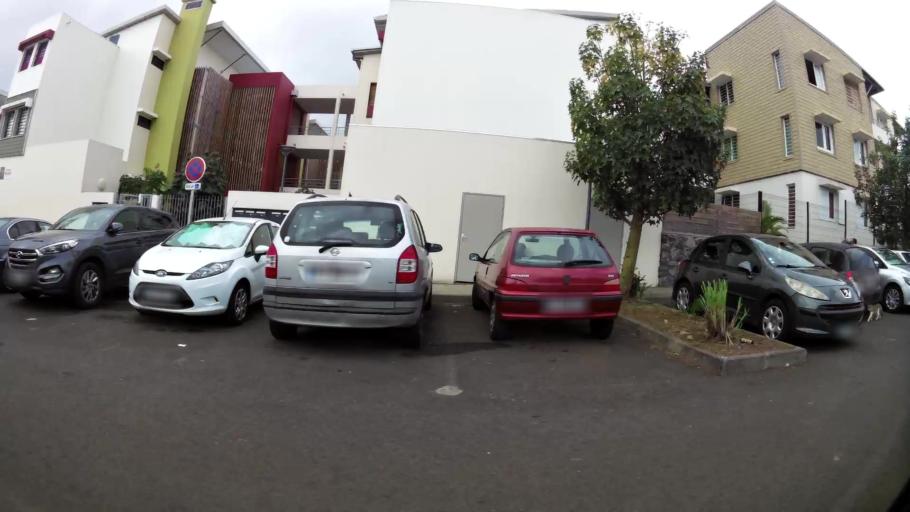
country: RE
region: Reunion
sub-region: Reunion
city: Sainte-Suzanne
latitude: -20.9010
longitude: 55.5976
